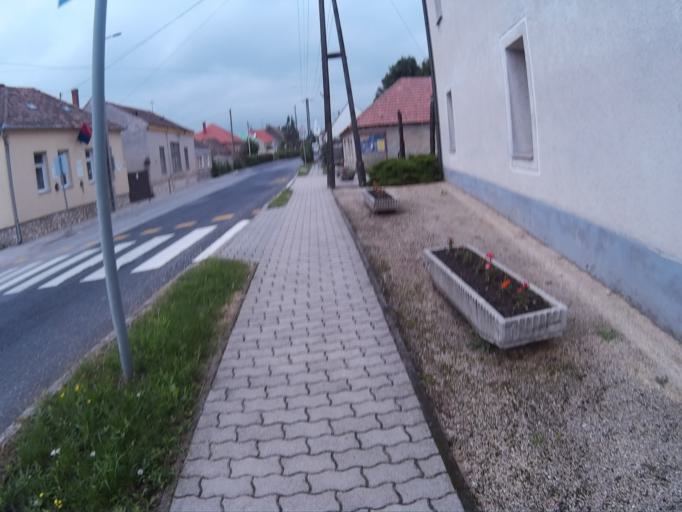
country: HU
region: Veszprem
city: Papa
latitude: 47.2815
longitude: 17.5213
